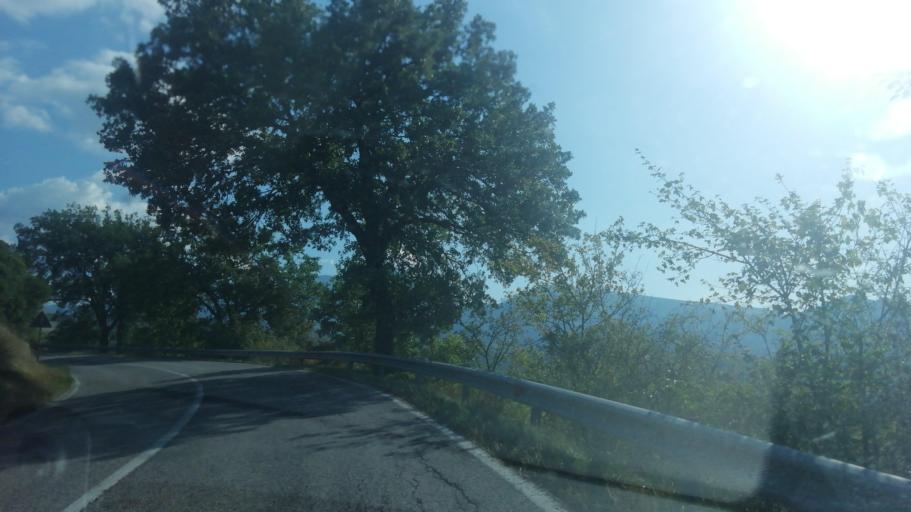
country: IT
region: The Marches
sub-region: Provincia di Pesaro e Urbino
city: Frontone
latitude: 43.5443
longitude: 12.7250
